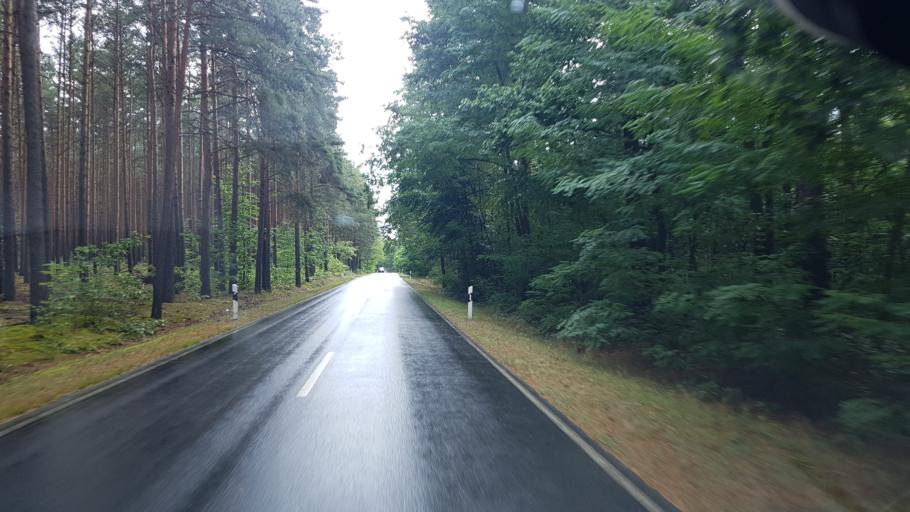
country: DE
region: Saxony
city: Gross Duben
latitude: 51.6332
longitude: 14.5471
